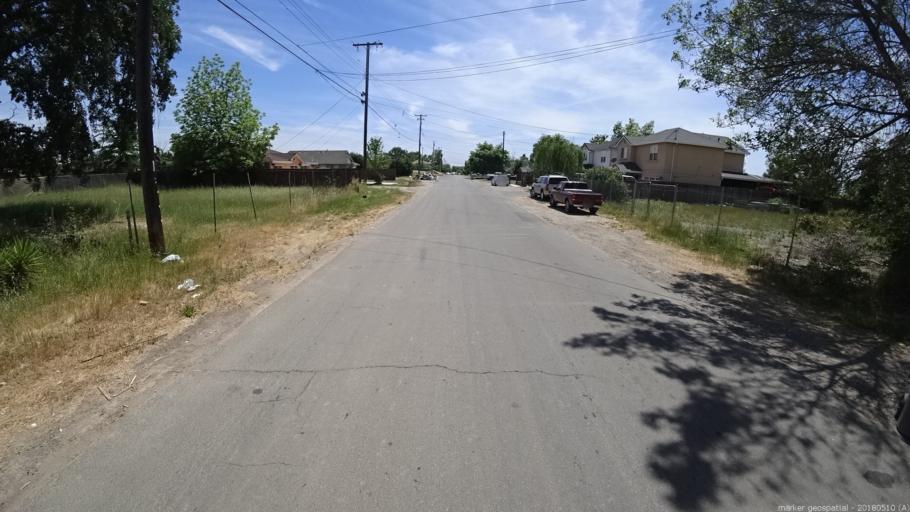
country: US
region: California
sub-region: Sacramento County
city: Rio Linda
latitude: 38.6305
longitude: -121.4526
